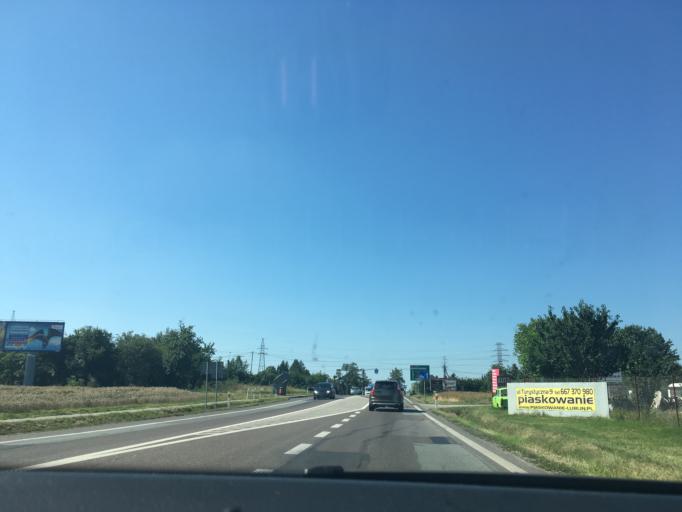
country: PL
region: Lublin Voivodeship
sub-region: Powiat lubelski
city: Jakubowice Murowane
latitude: 51.3122
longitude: 22.6001
